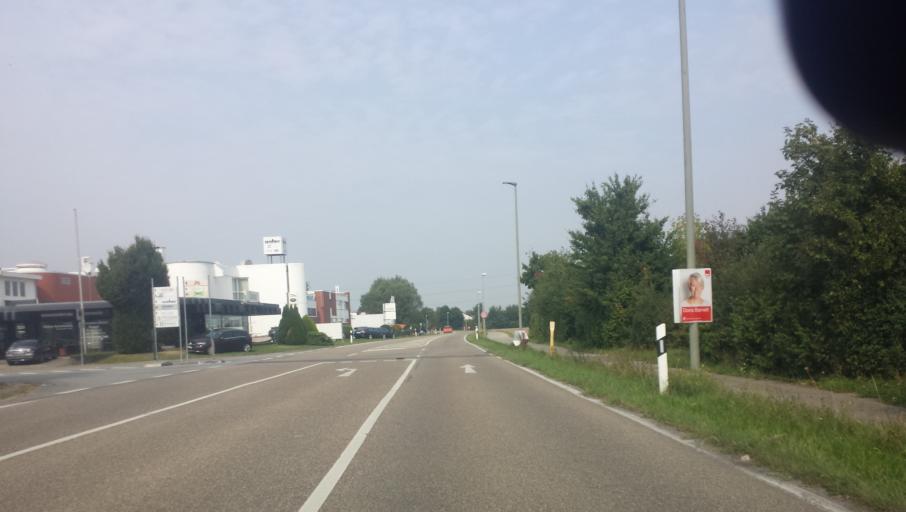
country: DE
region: Rheinland-Pfalz
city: Mutterstadt
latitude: 49.4256
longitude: 8.3658
